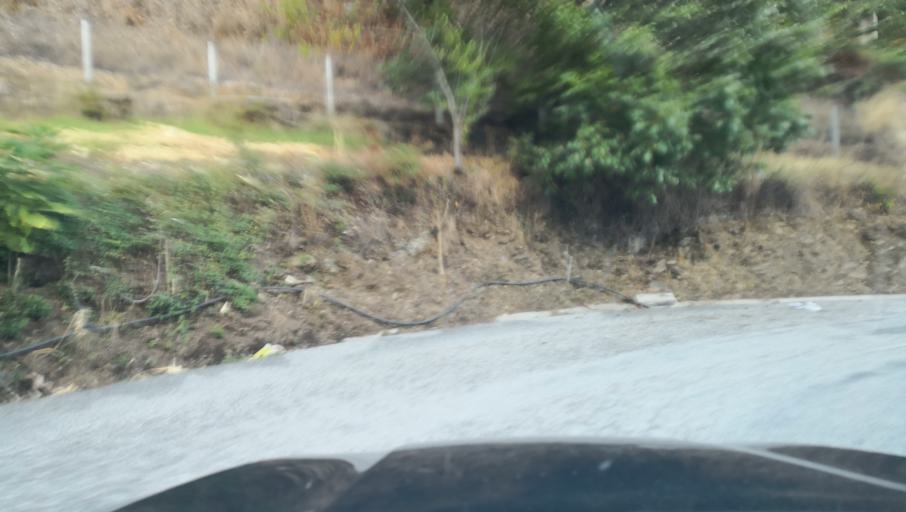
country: PT
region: Vila Real
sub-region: Santa Marta de Penaguiao
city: Santa Marta de Penaguiao
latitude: 41.2455
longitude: -7.8503
